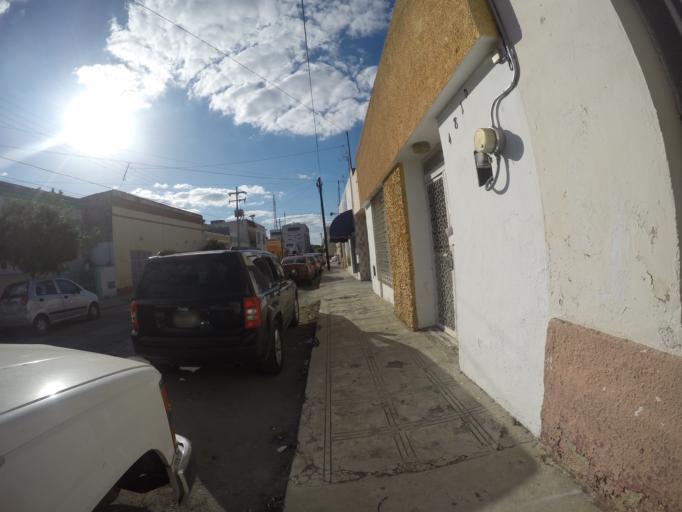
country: MX
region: Yucatan
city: Merida
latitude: 20.9786
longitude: -89.6163
